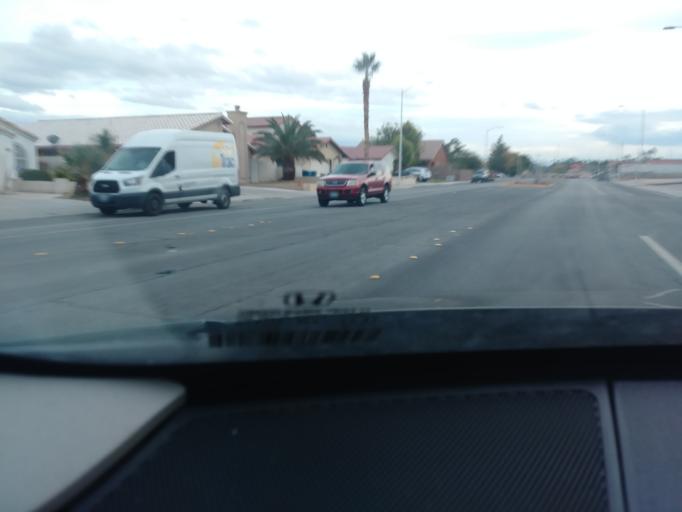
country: US
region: Nevada
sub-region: Clark County
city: Spring Valley
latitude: 36.1621
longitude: -115.2194
